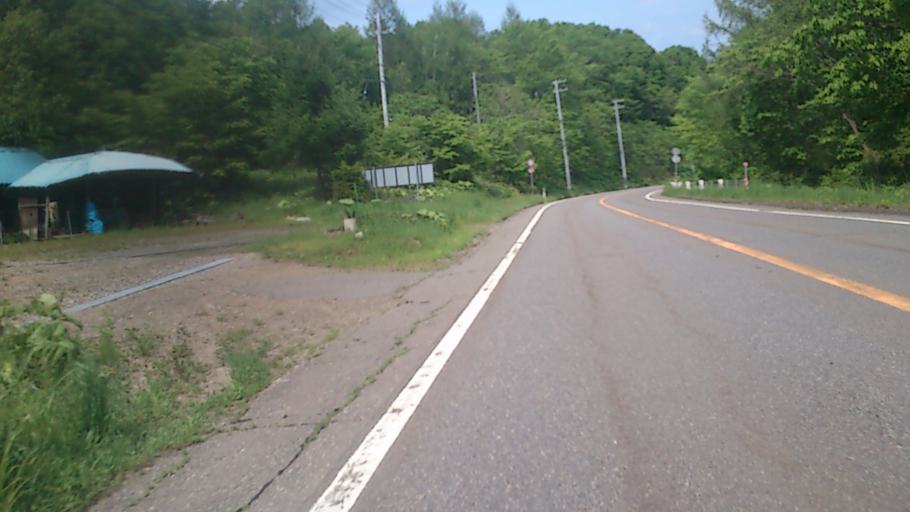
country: JP
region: Hokkaido
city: Kitami
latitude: 43.3068
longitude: 143.6950
